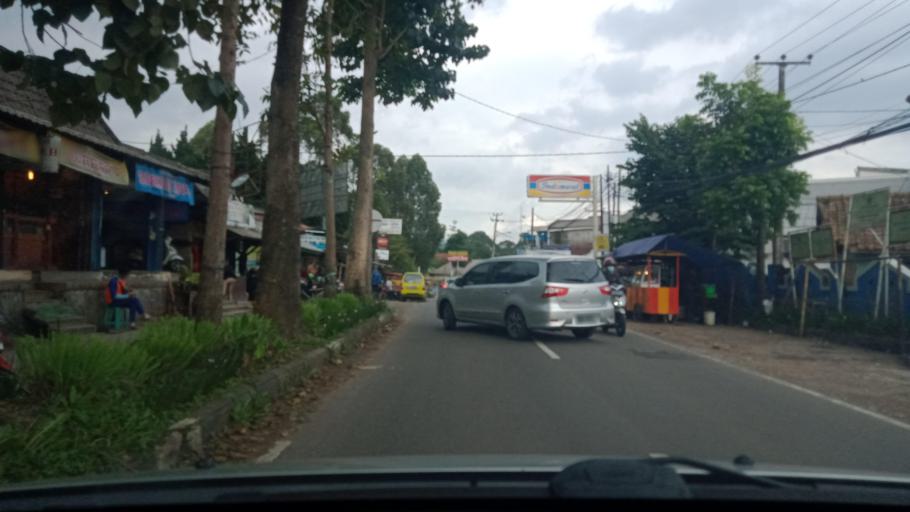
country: ID
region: West Java
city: Lembang
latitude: -6.8031
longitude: 107.5822
